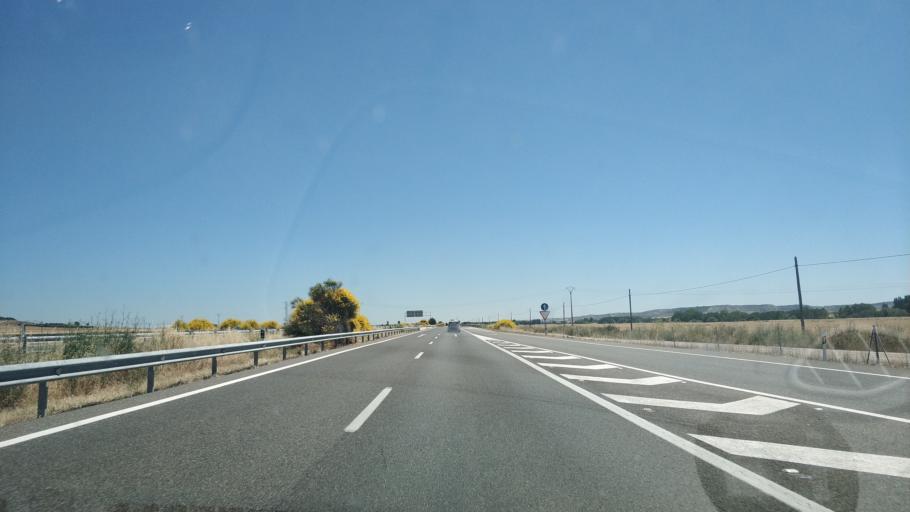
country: ES
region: Castille and Leon
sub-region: Provincia de Palencia
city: Palenzuela
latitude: 42.1201
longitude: -4.1494
